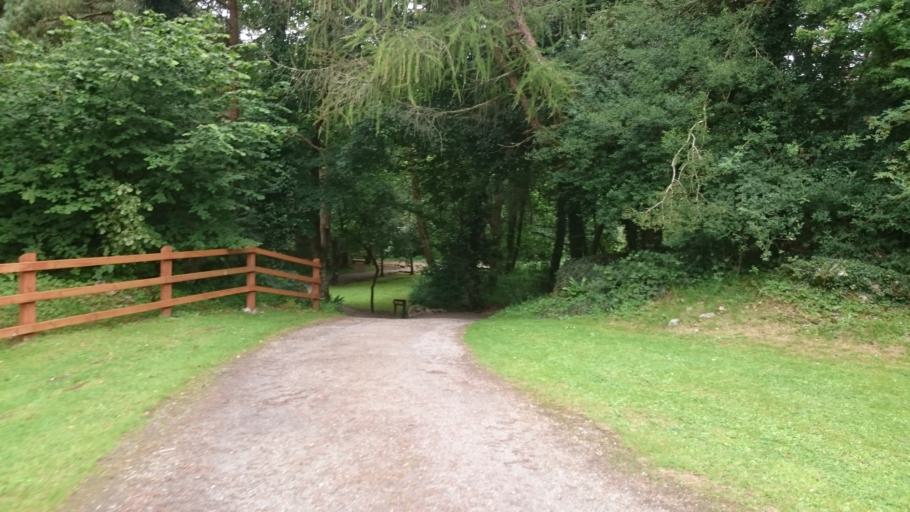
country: IE
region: Munster
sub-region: An Clar
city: Sixmilebridge
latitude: 52.8111
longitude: -8.7942
